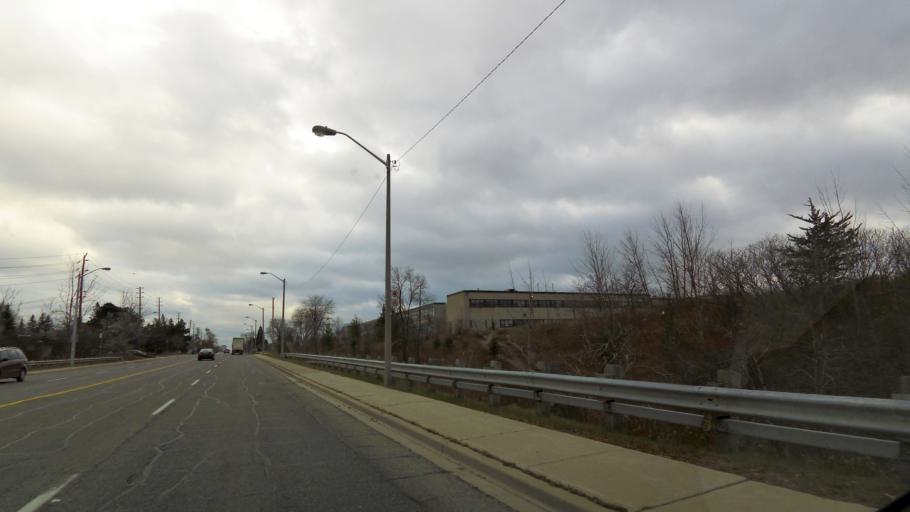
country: CA
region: Ontario
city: Etobicoke
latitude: 43.7292
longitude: -79.5618
